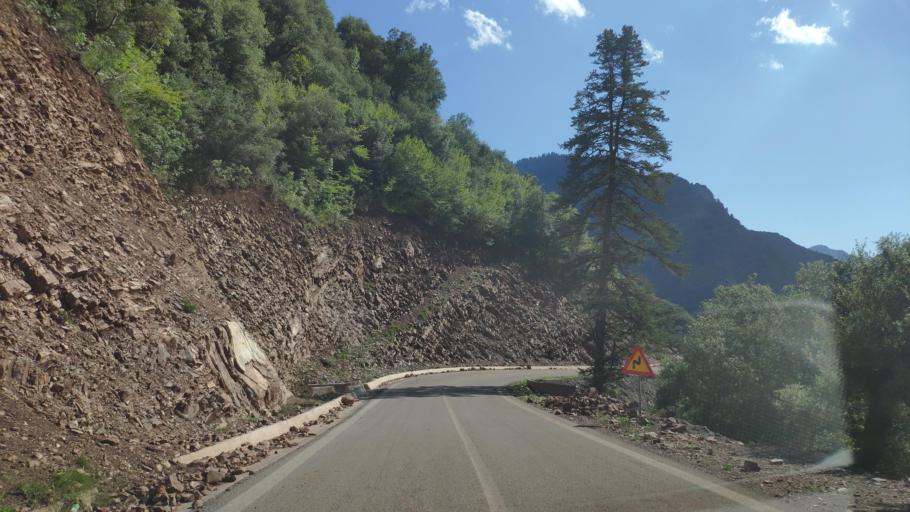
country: GR
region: Central Greece
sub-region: Nomos Evrytanias
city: Kerasochori
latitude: 39.1285
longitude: 21.6269
